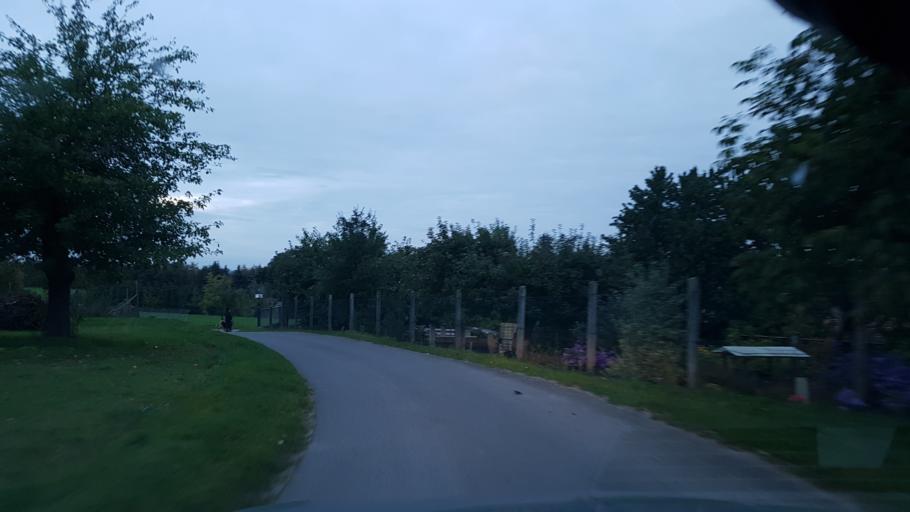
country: DE
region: Brandenburg
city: Hirschfeld
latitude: 51.3846
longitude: 13.6128
